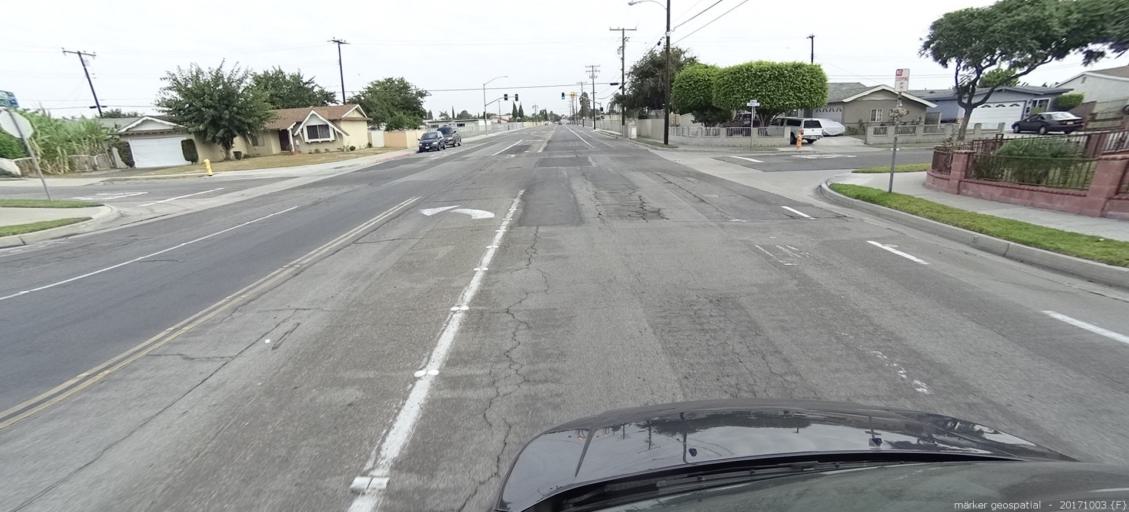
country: US
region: California
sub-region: Orange County
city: Garden Grove
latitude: 33.7480
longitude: -117.9462
